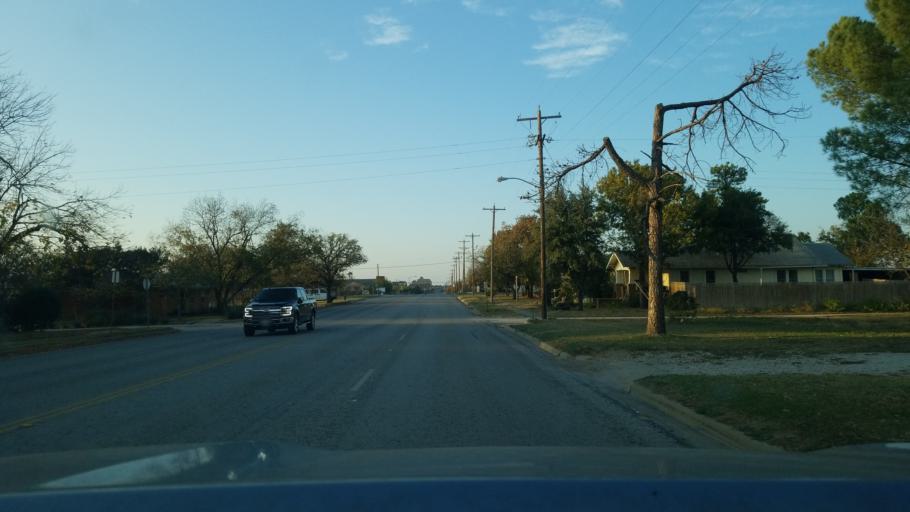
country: US
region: Texas
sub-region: Eastland County
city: Cisco
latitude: 32.3802
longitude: -98.9741
